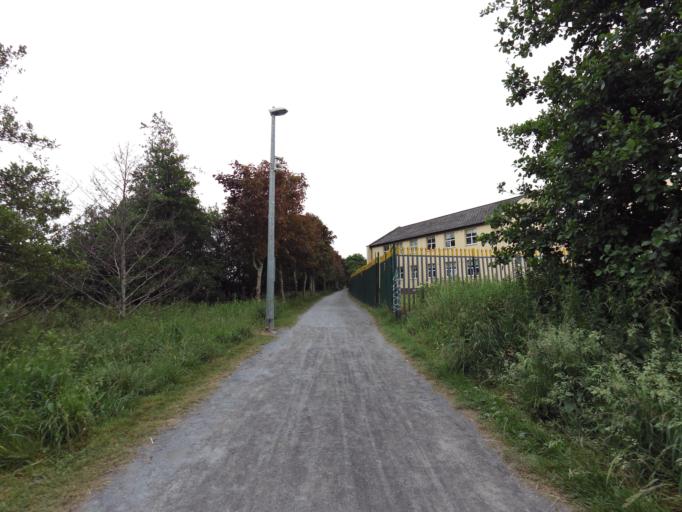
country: IE
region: Connaught
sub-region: County Galway
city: Gaillimh
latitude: 53.2897
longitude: -9.0657
